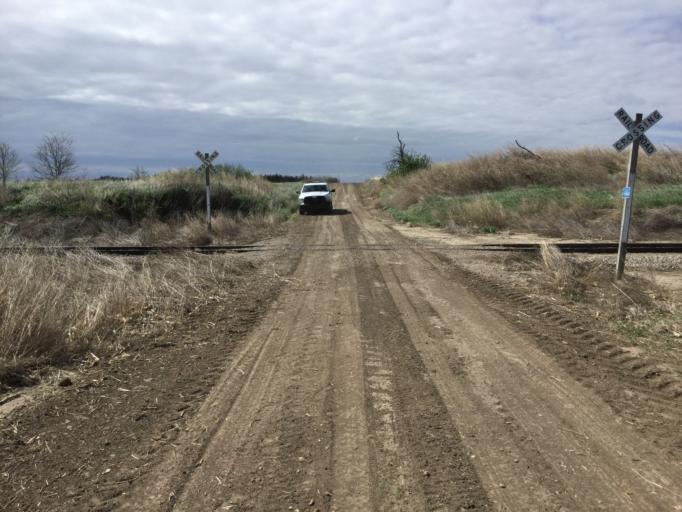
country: US
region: Kansas
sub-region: Phillips County
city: Phillipsburg
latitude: 39.7632
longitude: -99.2541
